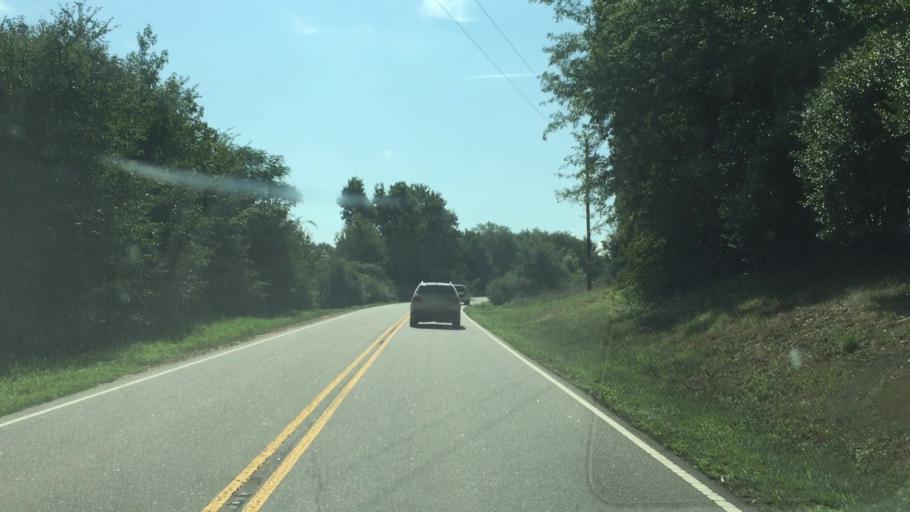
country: US
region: North Carolina
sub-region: Anson County
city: Burnsville
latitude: 35.0977
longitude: -80.3076
